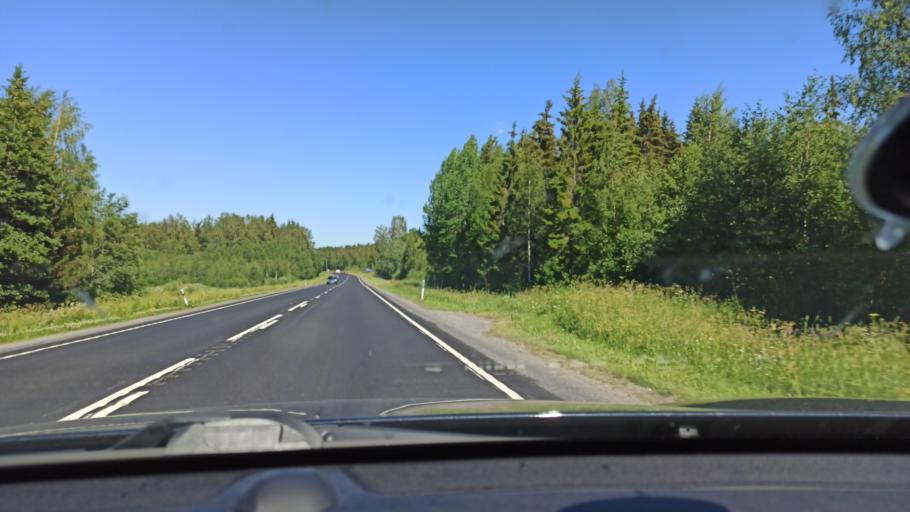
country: FI
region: Ostrobothnia
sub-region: Vaasa
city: Oravais
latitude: 63.2794
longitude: 22.3460
